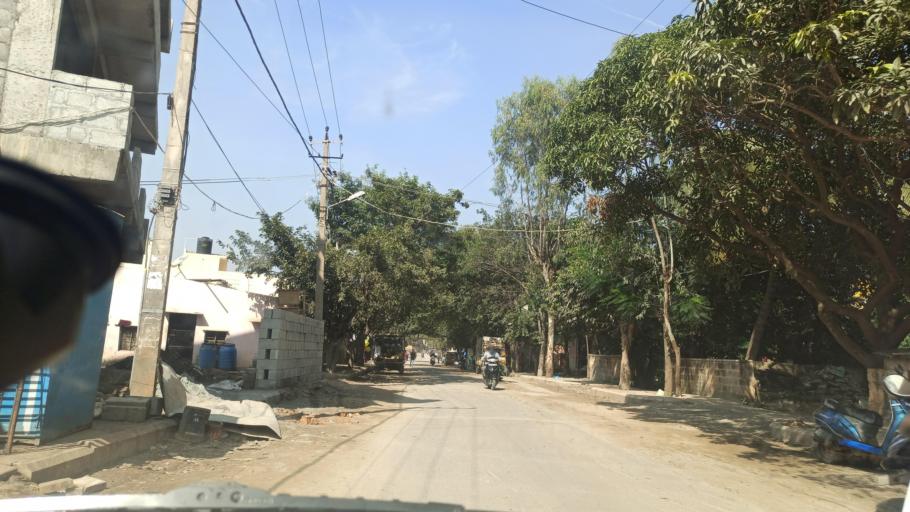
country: IN
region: Karnataka
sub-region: Bangalore Urban
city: Bangalore
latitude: 12.9248
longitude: 77.6942
